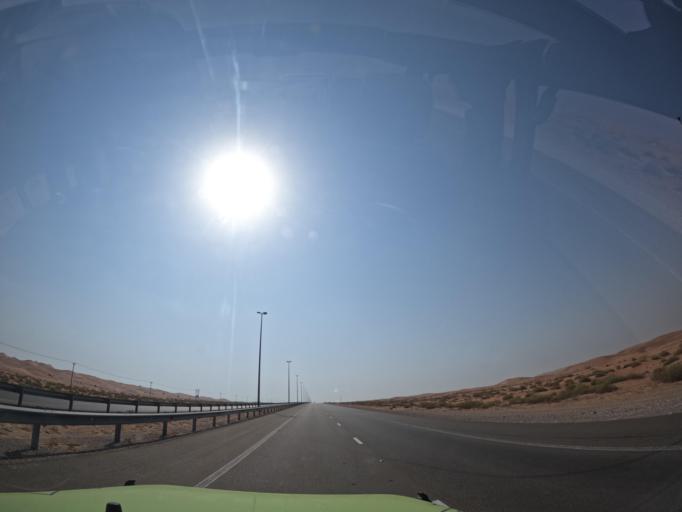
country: OM
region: Al Buraimi
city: Al Buraymi
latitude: 24.4314
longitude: 55.6766
